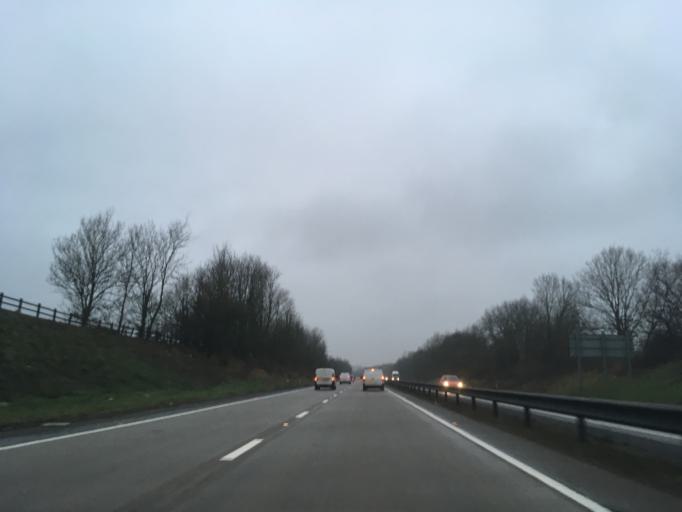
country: GB
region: Wales
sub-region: Cardiff
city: Radyr
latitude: 51.4842
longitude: -3.2845
